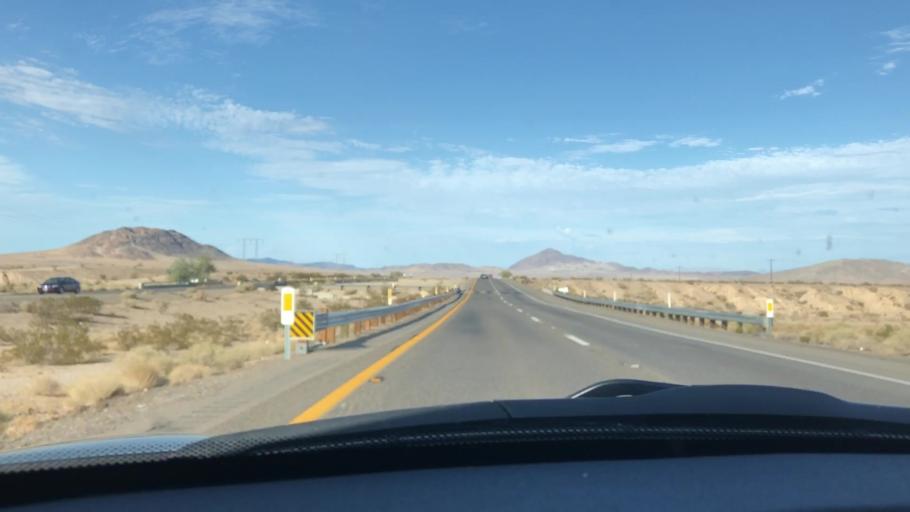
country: US
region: California
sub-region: San Bernardino County
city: Fort Irwin
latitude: 35.0171
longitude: -116.5138
